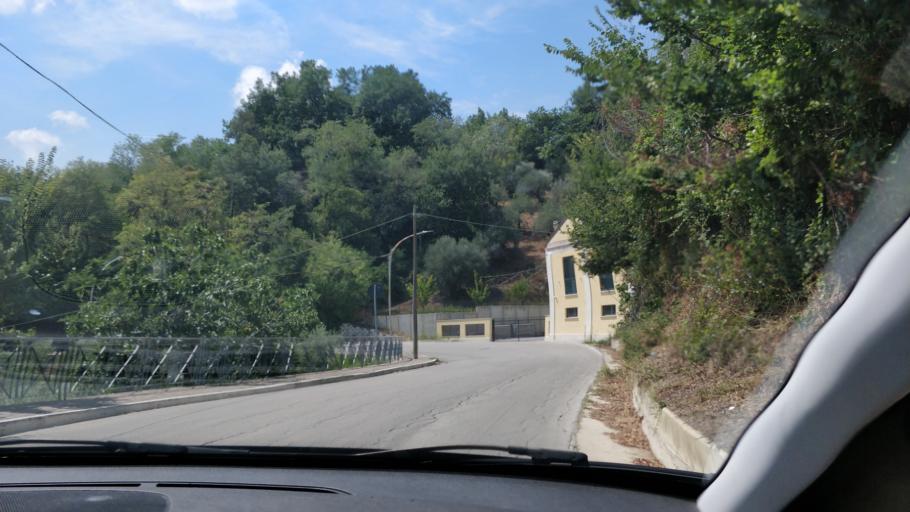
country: IT
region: Abruzzo
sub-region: Provincia di Chieti
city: Sambuceto
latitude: 42.4088
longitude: 14.2007
